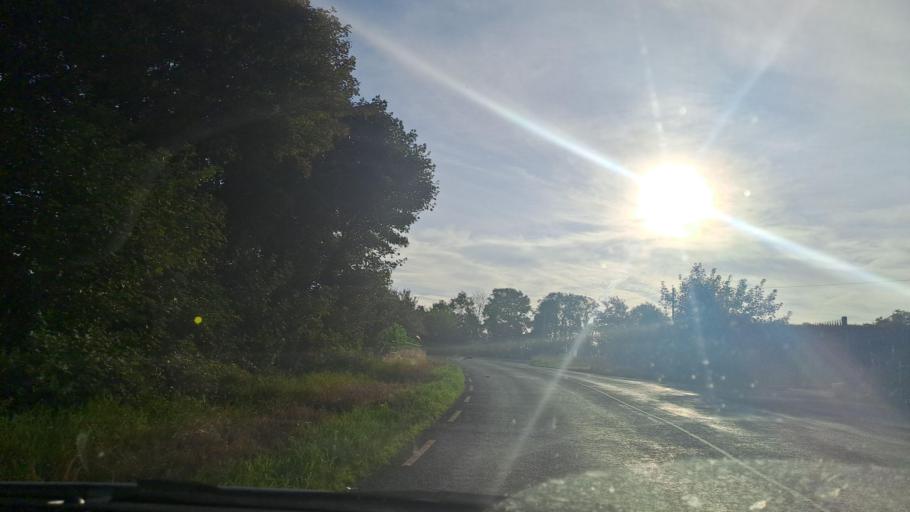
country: IE
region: Ulster
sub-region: An Cabhan
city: Bailieborough
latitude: 53.9892
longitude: -6.8866
